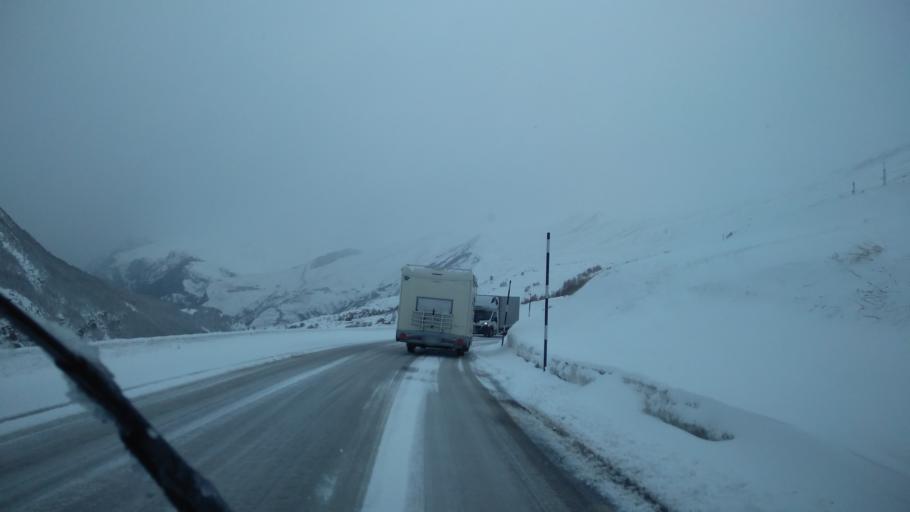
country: FR
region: Rhone-Alpes
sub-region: Departement de la Savoie
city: Valloire
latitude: 45.0373
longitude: 6.3648
